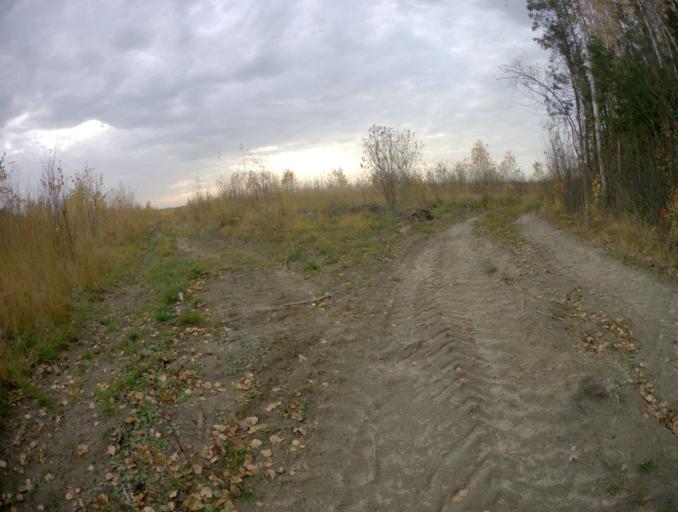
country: RU
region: Vladimir
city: Golovino
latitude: 55.9417
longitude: 40.3834
